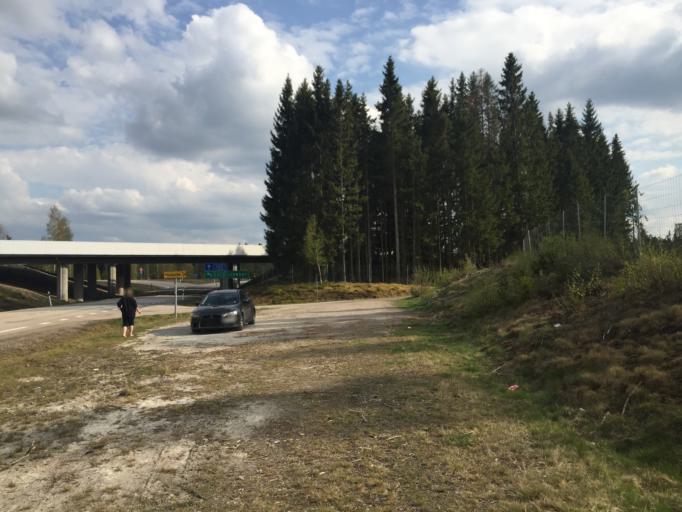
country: SE
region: Kronoberg
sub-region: Markaryds Kommun
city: Stromsnasbruk
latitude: 56.6234
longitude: 13.7824
